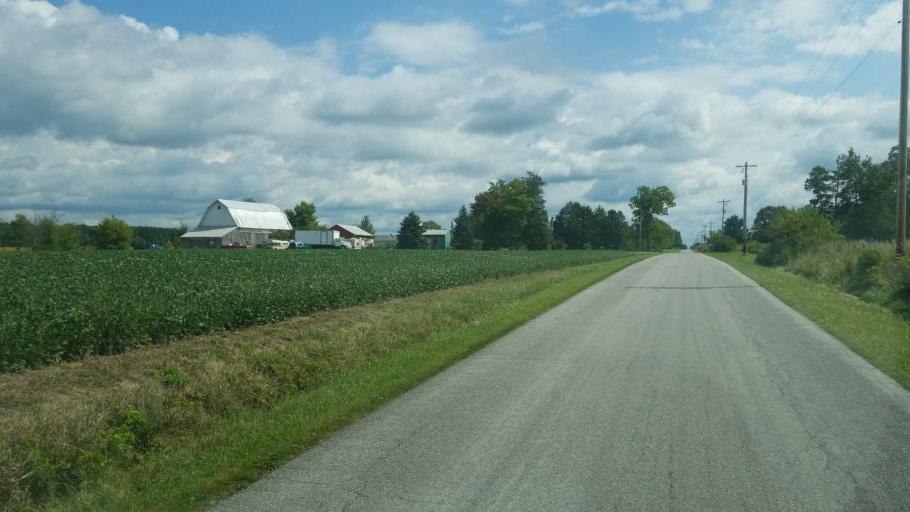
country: US
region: Ohio
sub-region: Sandusky County
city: Green Springs
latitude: 41.0957
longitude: -83.0094
